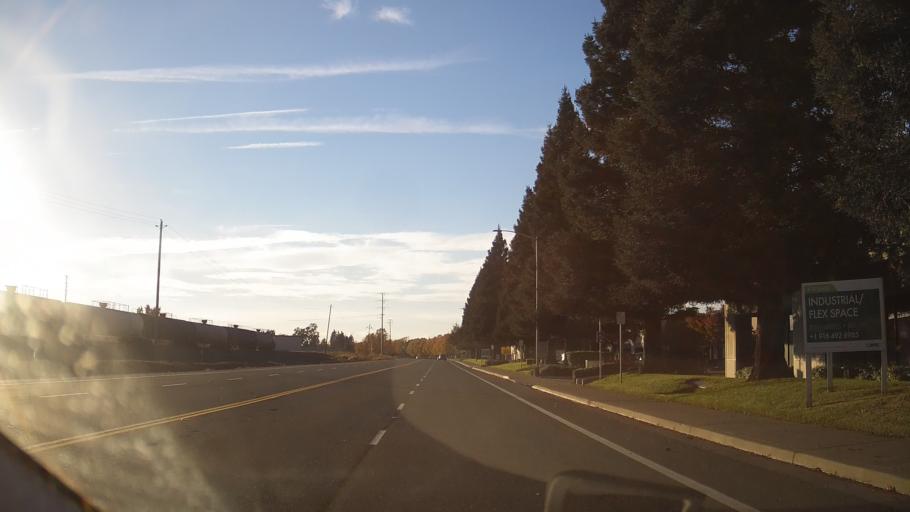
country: US
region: California
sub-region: Yolo County
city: West Sacramento
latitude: 38.5737
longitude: -121.5590
